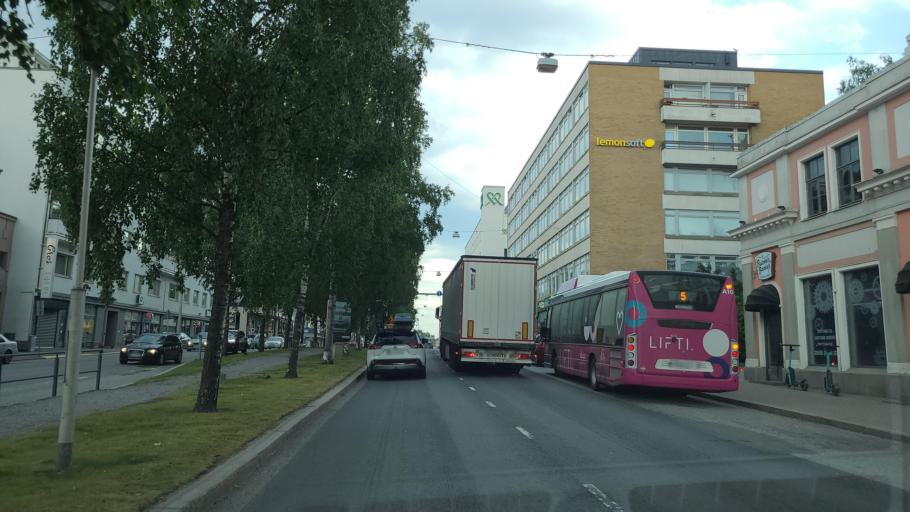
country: FI
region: Ostrobothnia
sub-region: Vaasa
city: Vaasa
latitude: 63.0953
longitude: 21.6175
